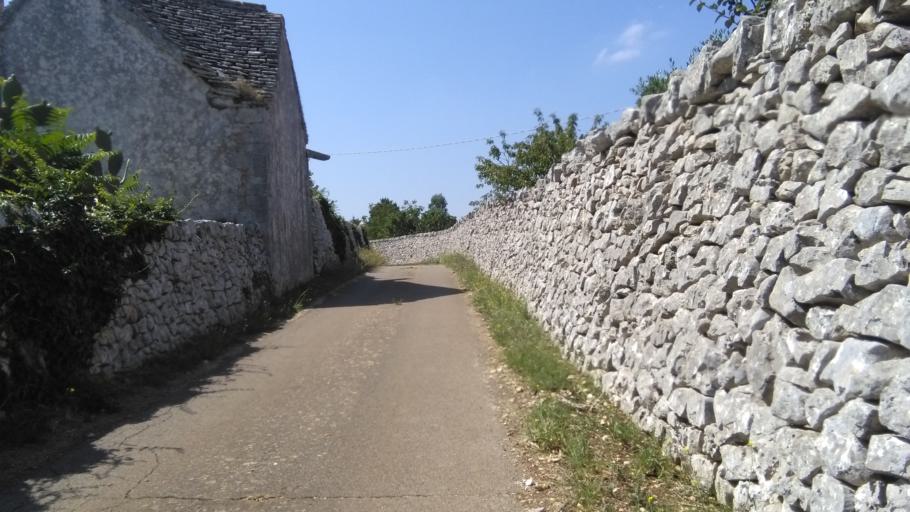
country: IT
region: Apulia
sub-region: Provincia di Bari
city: Putignano
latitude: 40.8253
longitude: 17.1396
